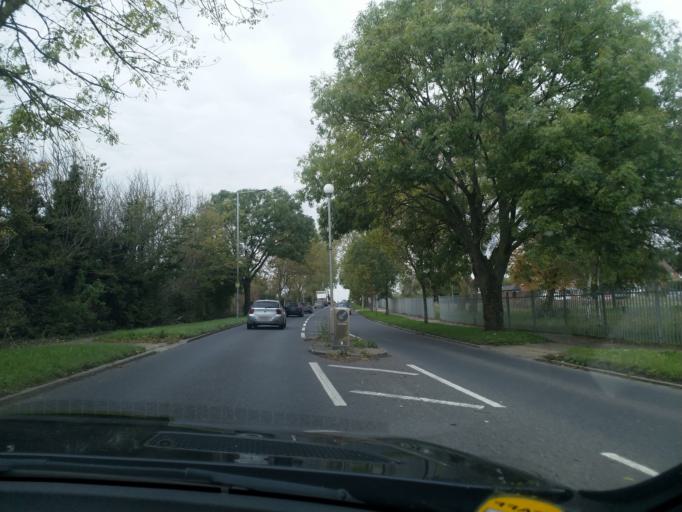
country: GB
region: England
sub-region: Greater London
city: Northolt
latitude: 51.5399
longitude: -0.3970
